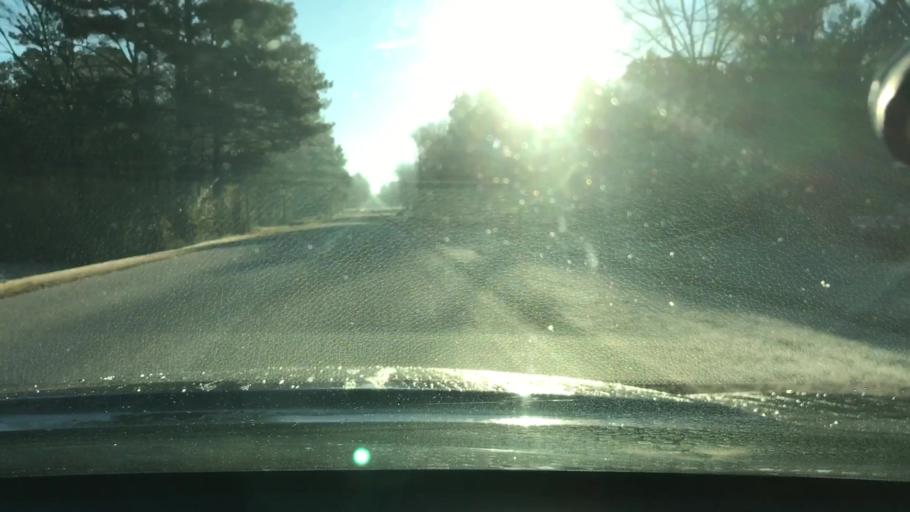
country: US
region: Alabama
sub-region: Talladega County
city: Mignon
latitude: 33.2118
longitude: -86.2976
